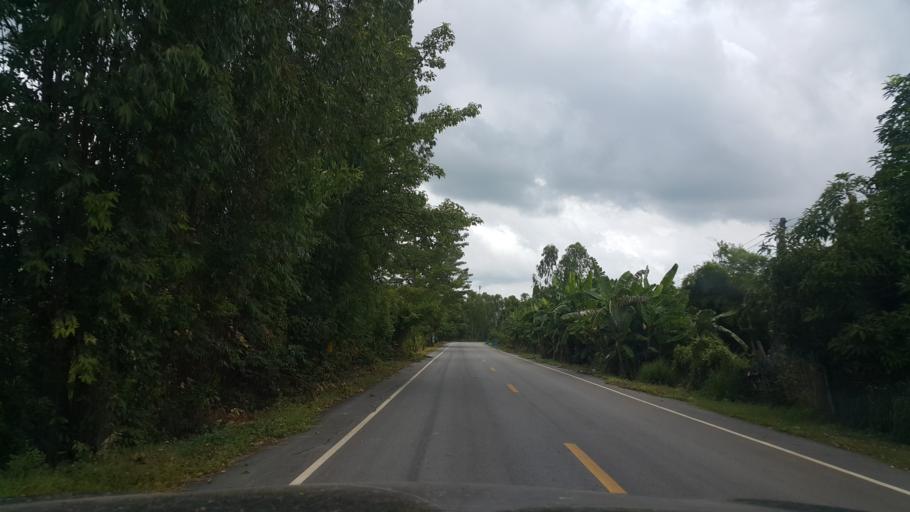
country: TH
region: Sukhothai
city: Kong Krailat
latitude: 16.9109
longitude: 99.8862
